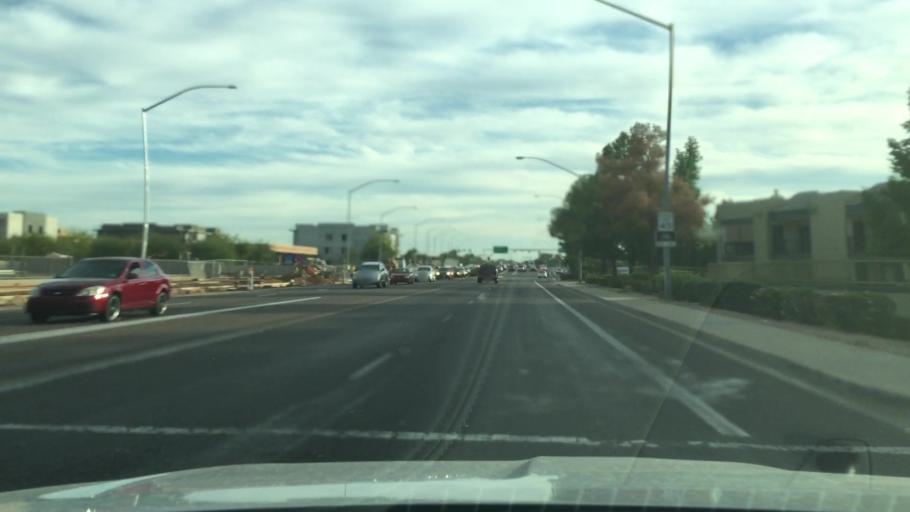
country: US
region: Arizona
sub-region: Maricopa County
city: Gilbert
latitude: 33.3900
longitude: -111.7539
